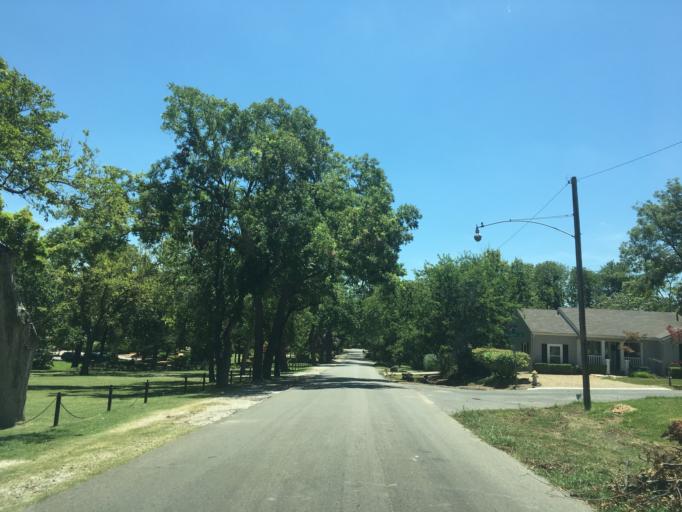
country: US
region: Texas
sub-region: Dallas County
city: Highland Park
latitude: 32.8453
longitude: -96.7091
